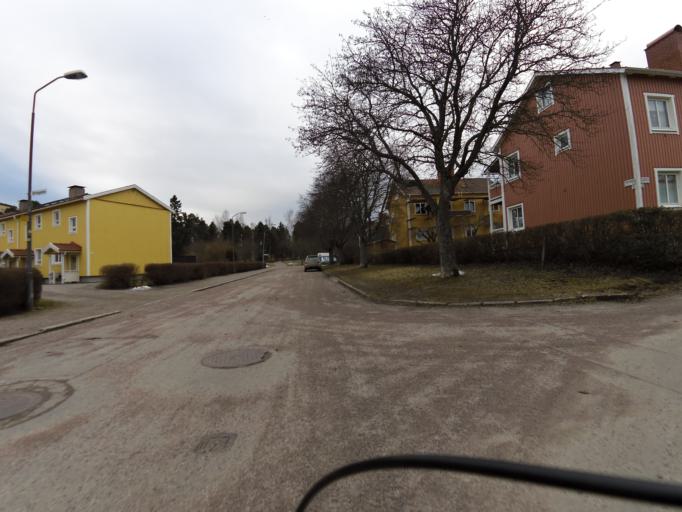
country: SE
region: Gaevleborg
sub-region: Gavle Kommun
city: Gavle
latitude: 60.6626
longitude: 17.1472
